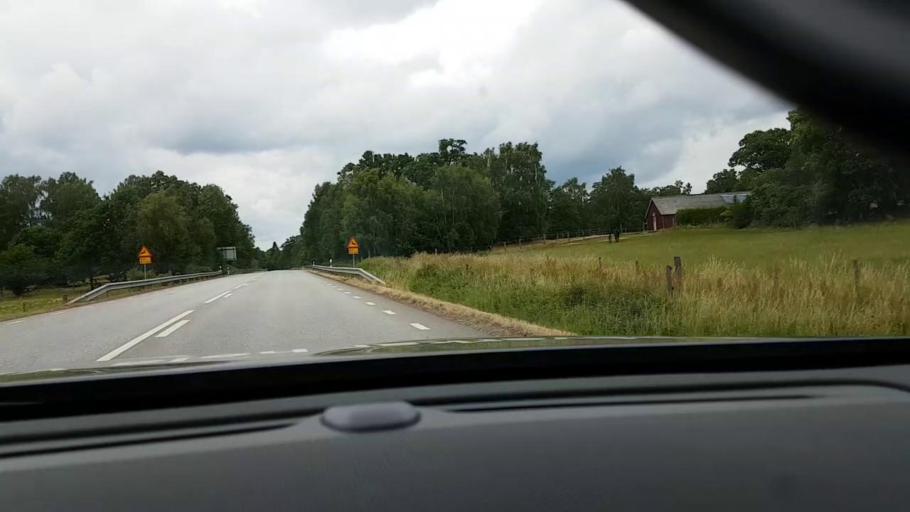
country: SE
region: Skane
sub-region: Horby Kommun
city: Hoerby
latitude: 55.8628
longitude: 13.6389
